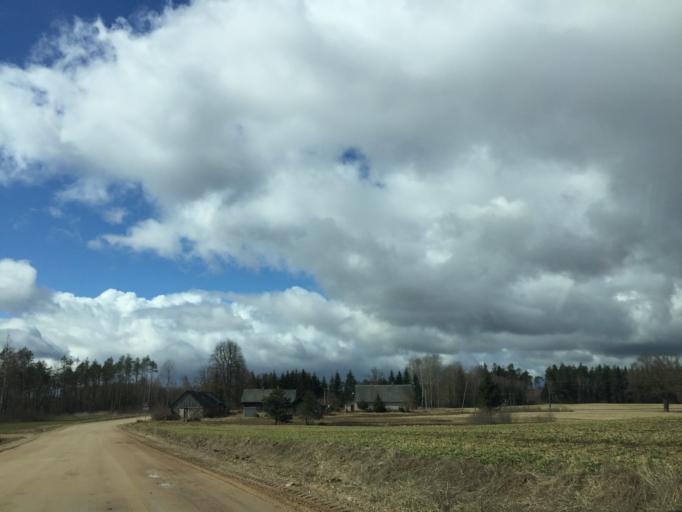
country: LV
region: Akniste
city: Akniste
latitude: 56.1057
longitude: 25.9380
